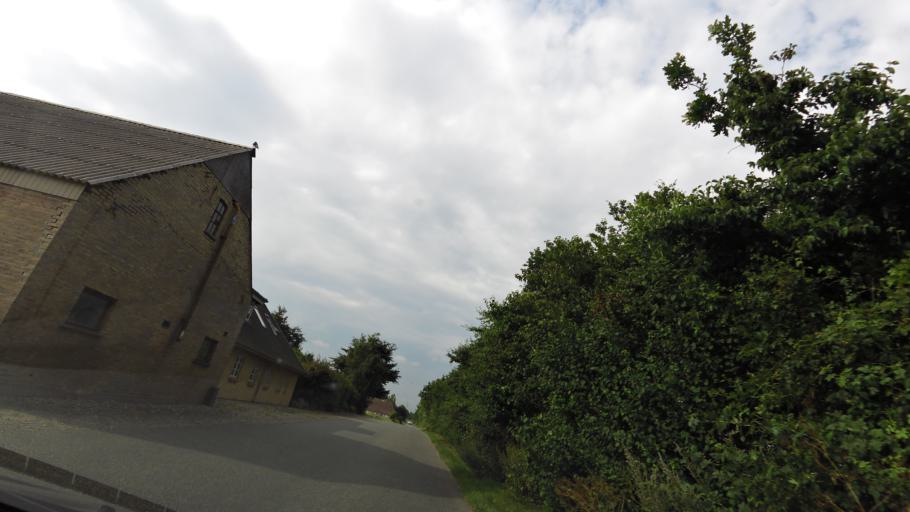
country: DK
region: South Denmark
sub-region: Nordfyns Kommune
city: Otterup
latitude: 55.5645
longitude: 10.4259
